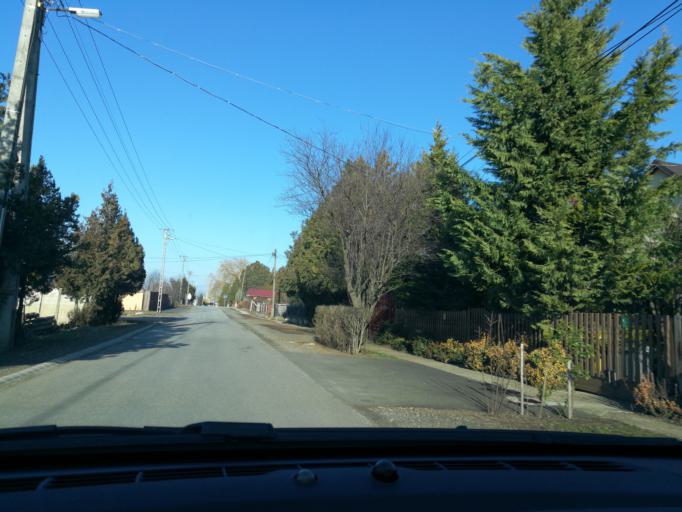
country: HU
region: Szabolcs-Szatmar-Bereg
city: Nyiregyhaza
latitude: 47.9494
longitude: 21.7532
